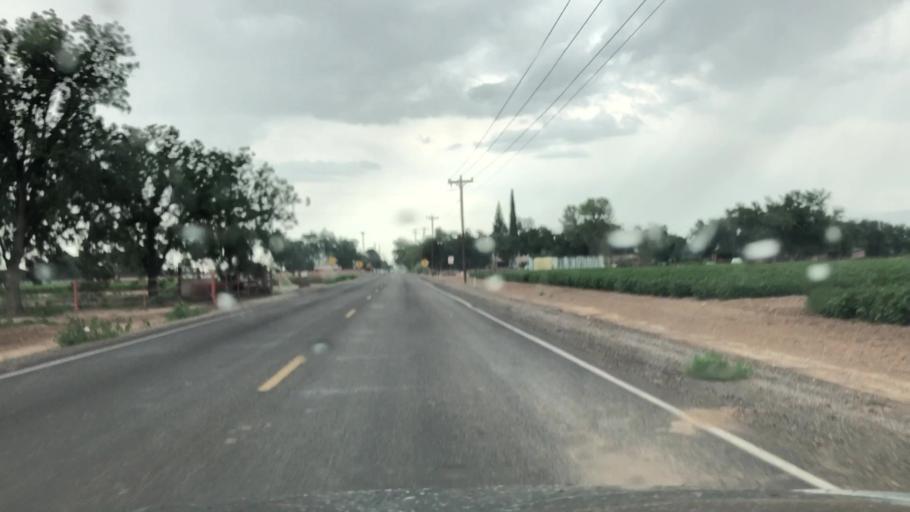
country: US
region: New Mexico
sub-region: Dona Ana County
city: Vado
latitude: 32.1089
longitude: -106.6835
